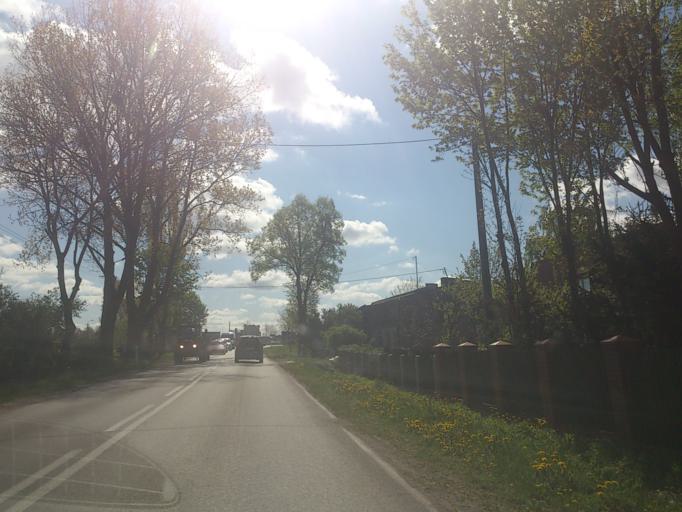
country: PL
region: Warmian-Masurian Voivodeship
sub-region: Powiat dzialdowski
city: Dzialdowo
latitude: 53.2266
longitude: 20.1979
